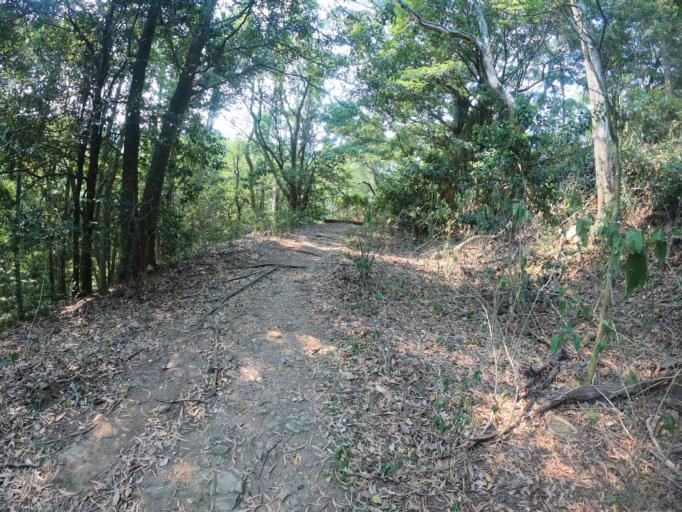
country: AU
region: New South Wales
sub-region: Wollongong
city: Bulli
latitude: -34.3020
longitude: 150.8821
